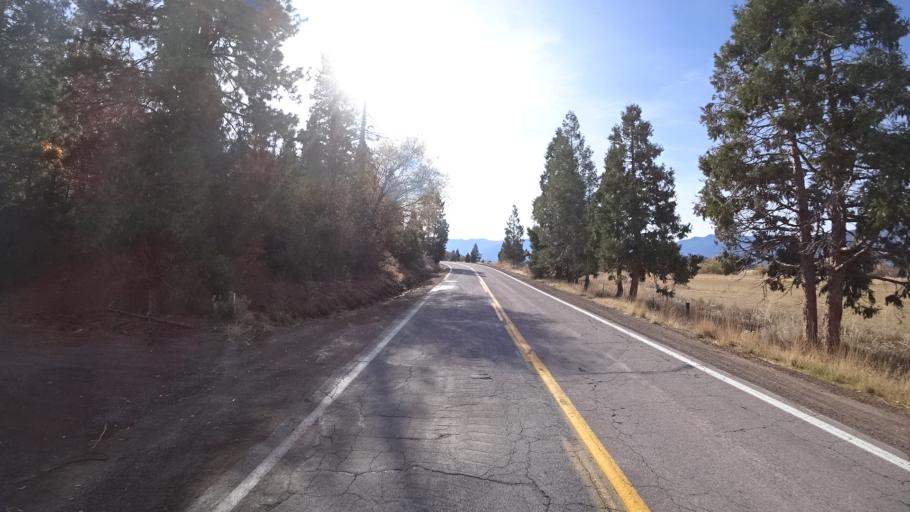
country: US
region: California
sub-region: Siskiyou County
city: Weed
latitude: 41.4805
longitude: -122.4107
